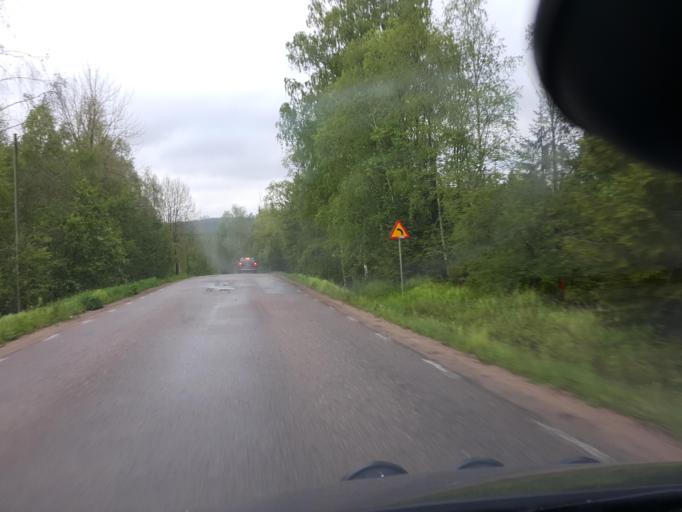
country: SE
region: Gaevleborg
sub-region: Ljusdals Kommun
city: Jaervsoe
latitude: 61.7875
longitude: 16.2176
